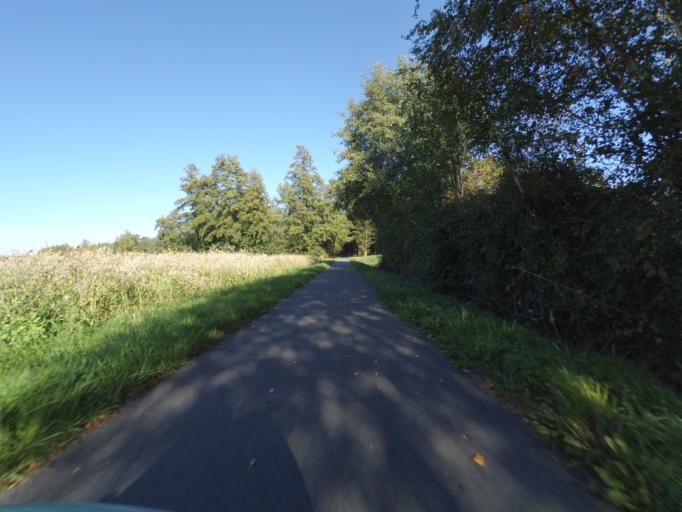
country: DE
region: North Rhine-Westphalia
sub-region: Regierungsbezirk Dusseldorf
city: Bocholt
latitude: 51.8817
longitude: 6.6039
